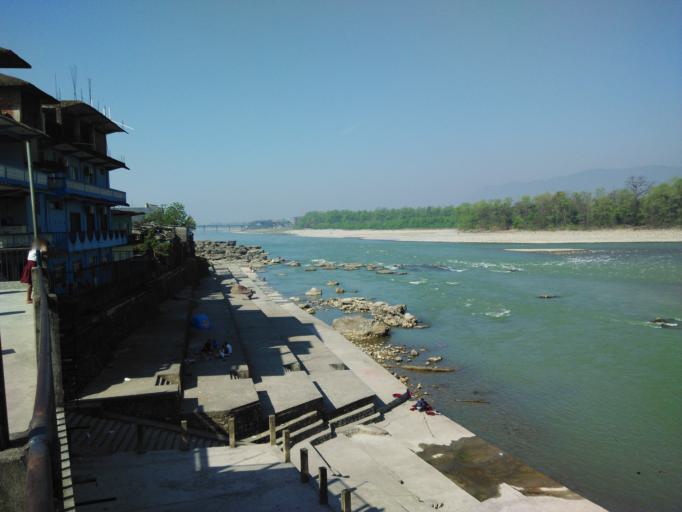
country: NP
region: Central Region
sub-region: Narayani Zone
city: Bharatpur
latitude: 27.7043
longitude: 84.4318
